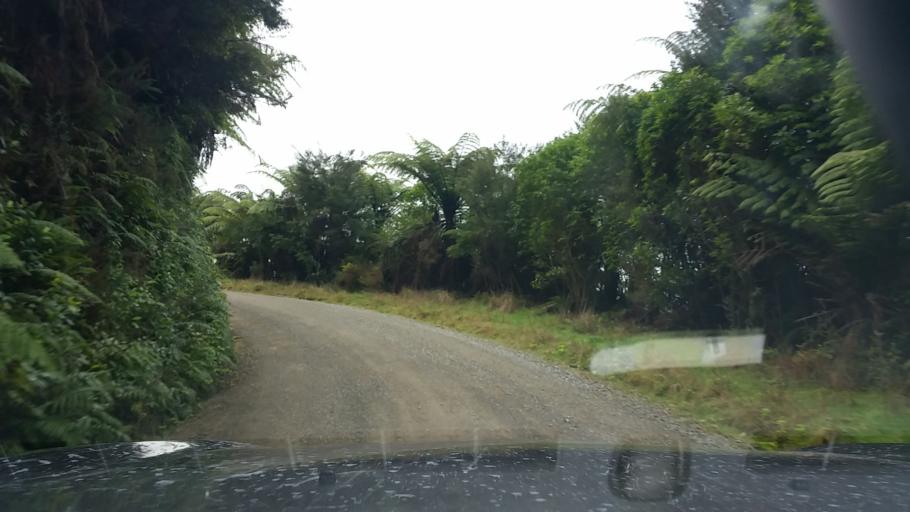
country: NZ
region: Marlborough
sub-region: Marlborough District
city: Picton
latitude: -41.1656
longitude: 173.9643
